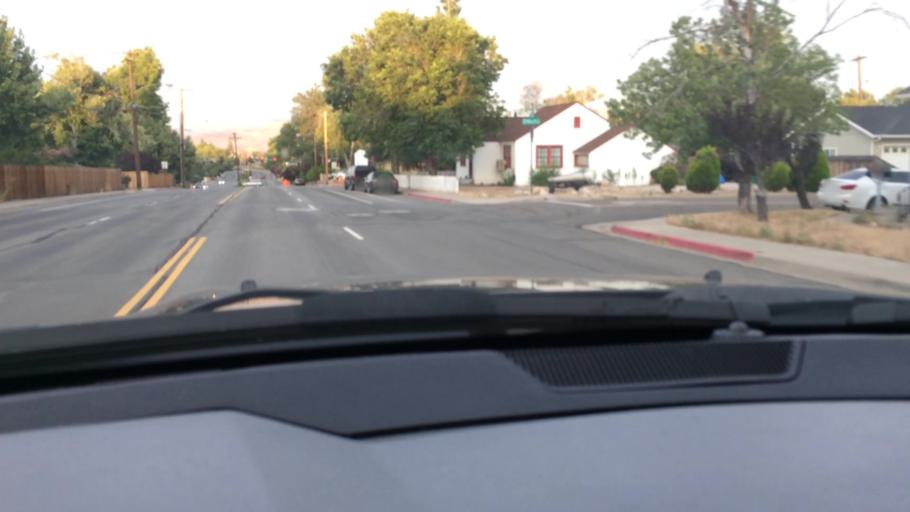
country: US
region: Nevada
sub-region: Washoe County
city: Reno
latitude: 39.5054
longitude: -119.8195
